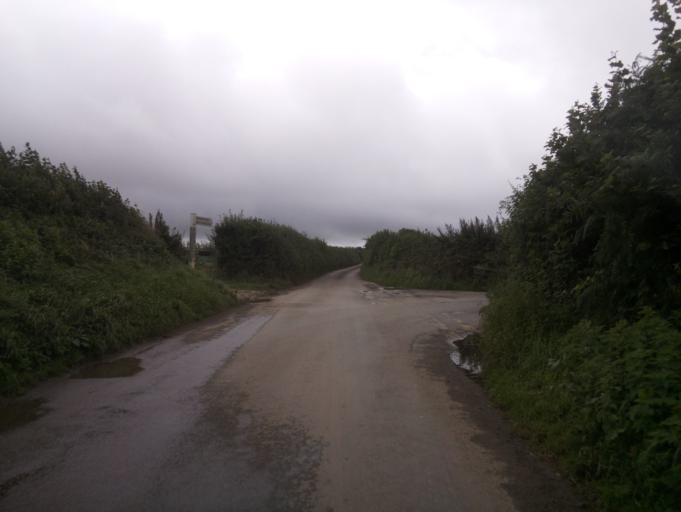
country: GB
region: England
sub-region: Devon
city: Kingsbridge
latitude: 50.3066
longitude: -3.7167
